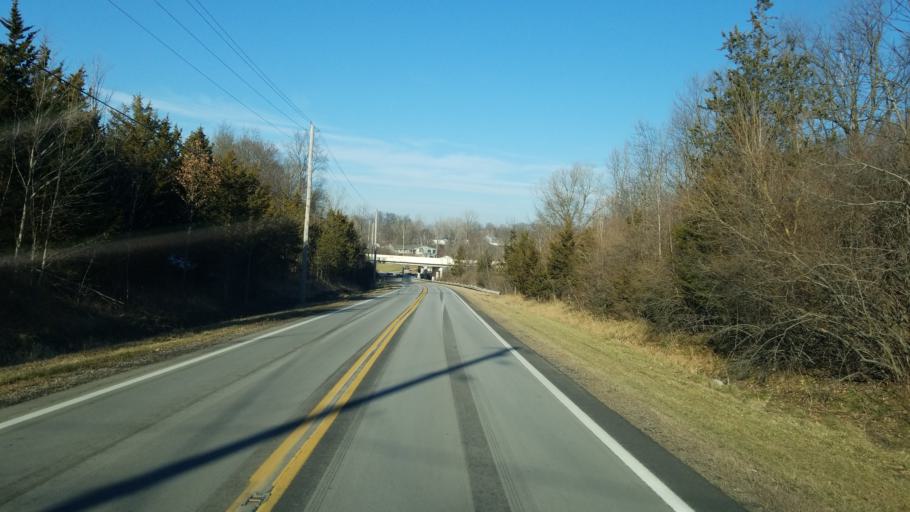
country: US
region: Ohio
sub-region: Huron County
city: Norwalk
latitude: 41.2227
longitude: -82.6410
